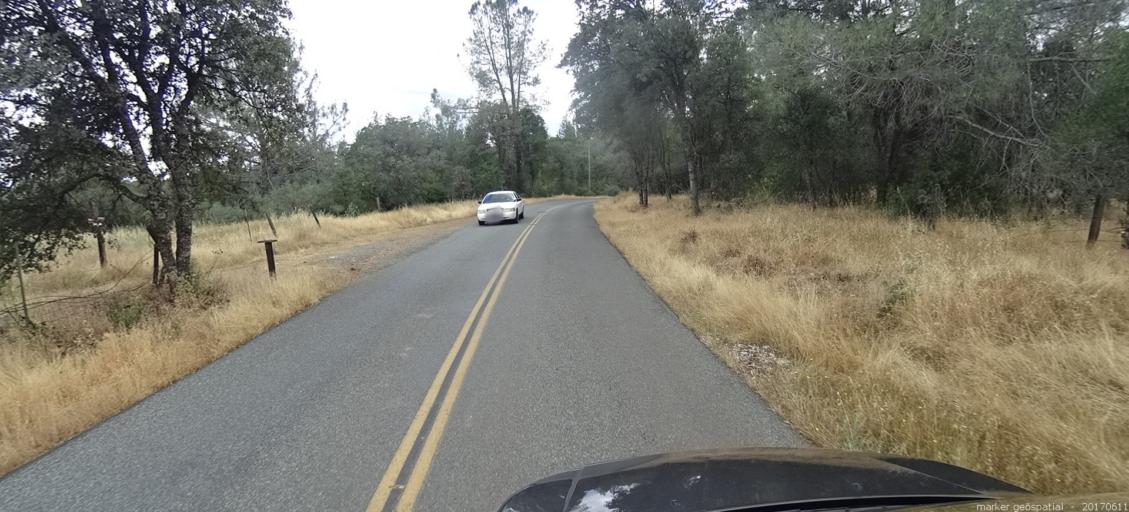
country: US
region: California
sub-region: Butte County
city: Berry Creek
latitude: 39.6447
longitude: -121.5314
